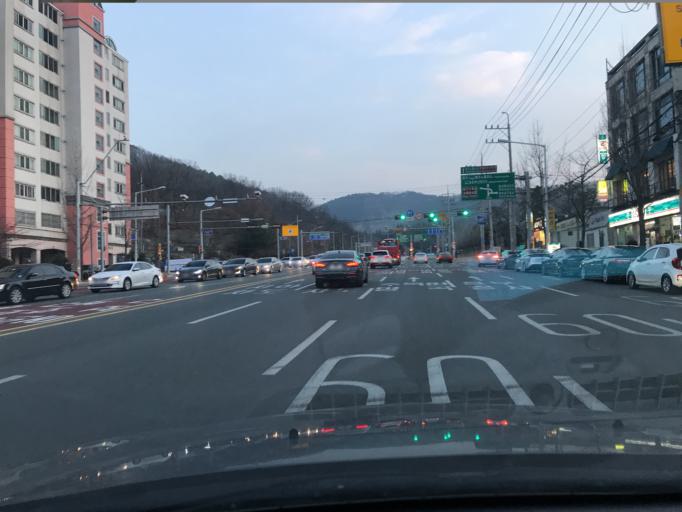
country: KR
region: Daegu
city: Hwawon
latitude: 35.8072
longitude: 128.5205
